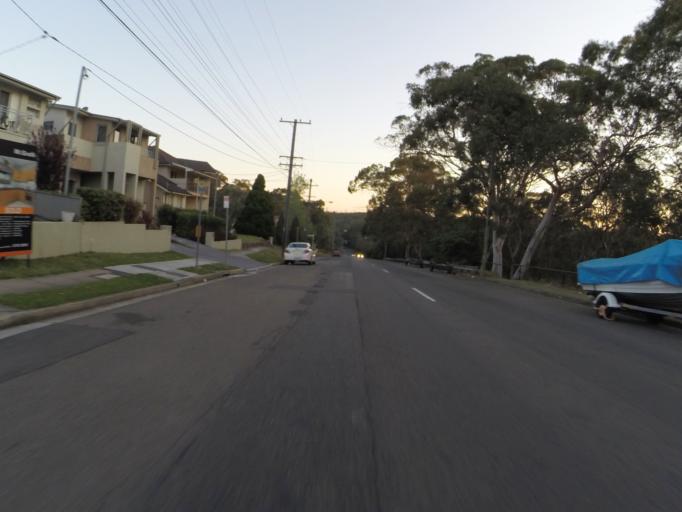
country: AU
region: New South Wales
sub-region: Bankstown
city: Revesby
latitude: -33.9663
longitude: 151.0155
